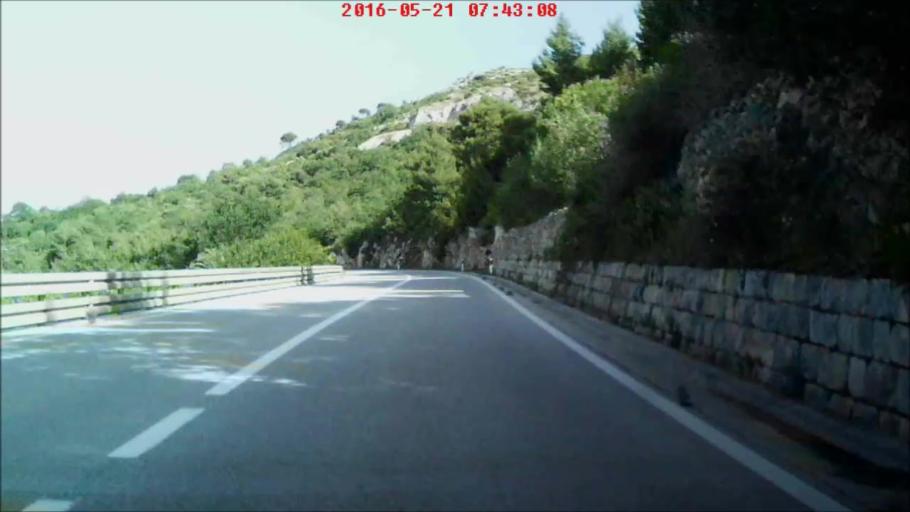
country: HR
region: Dubrovacko-Neretvanska
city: Podgora
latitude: 42.8114
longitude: 17.7934
